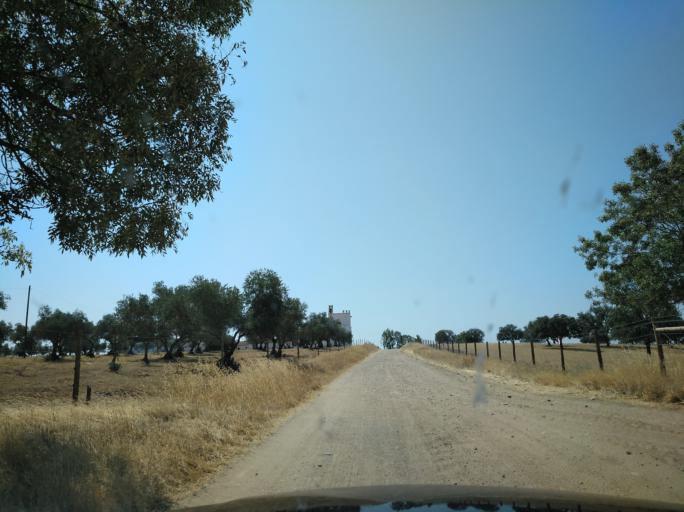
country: PT
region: Portalegre
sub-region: Campo Maior
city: Campo Maior
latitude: 39.0232
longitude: -6.9783
